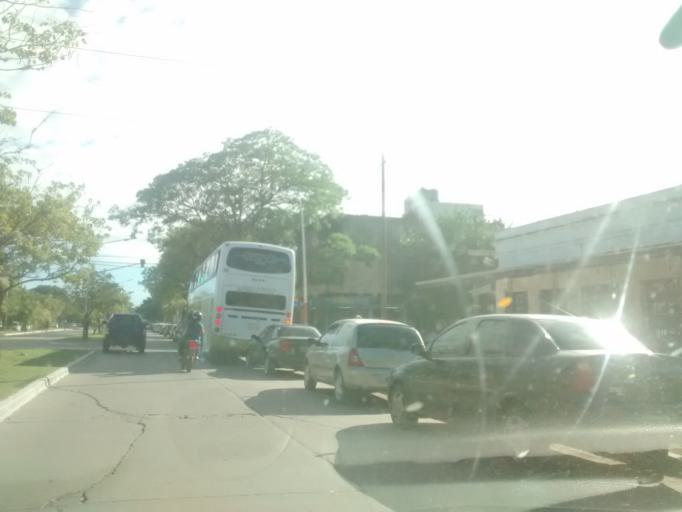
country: AR
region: Chaco
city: Resistencia
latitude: -27.4593
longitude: -58.9814
